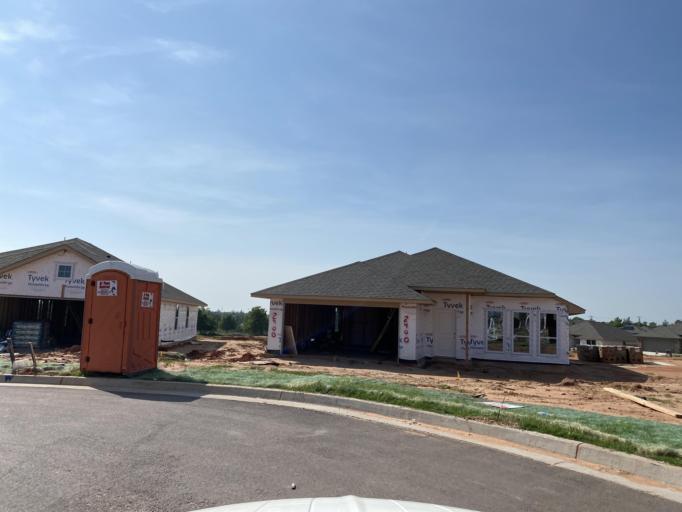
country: US
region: Oklahoma
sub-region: Oklahoma County
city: Midwest City
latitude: 35.4392
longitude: -97.3432
